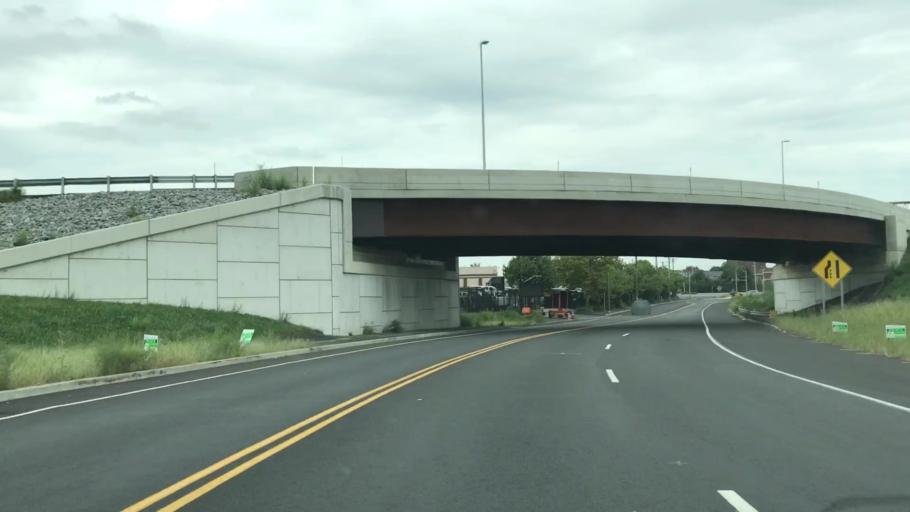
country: US
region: New Jersey
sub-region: Hudson County
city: Bayonne
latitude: 40.6787
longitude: -74.0969
